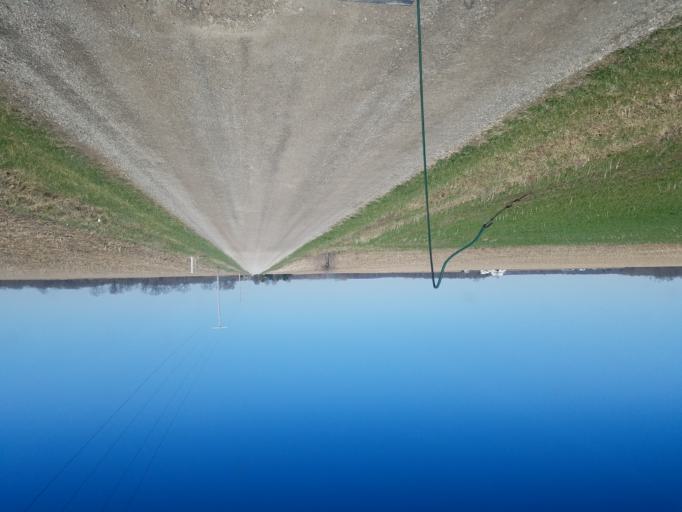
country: US
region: Ohio
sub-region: Morrow County
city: Cardington
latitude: 40.5868
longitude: -82.9080
